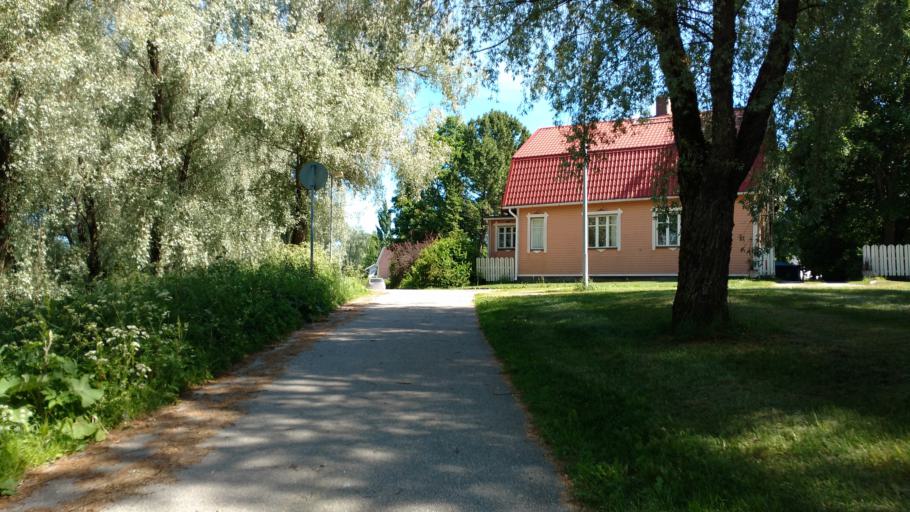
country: FI
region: Varsinais-Suomi
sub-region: Salo
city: Salo
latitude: 60.3900
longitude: 23.1304
